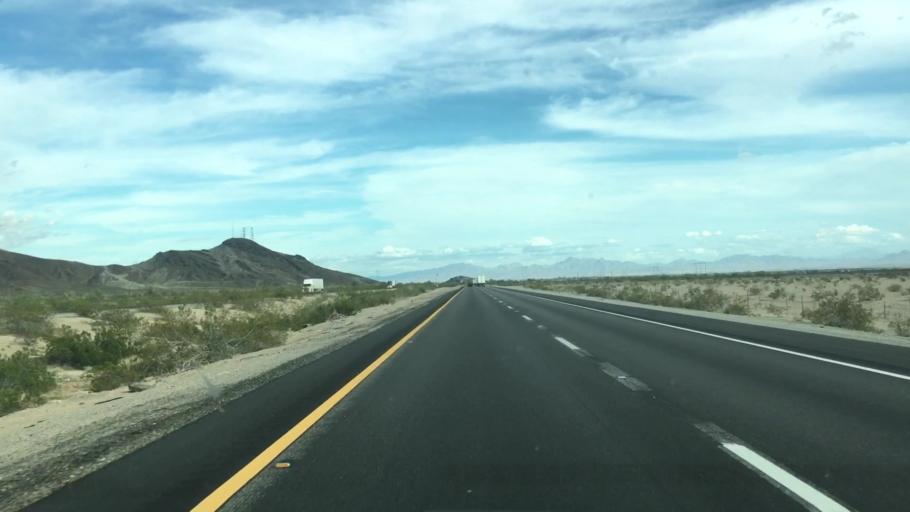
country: US
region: California
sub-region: Riverside County
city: Mesa Verde
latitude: 33.6098
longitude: -114.7891
